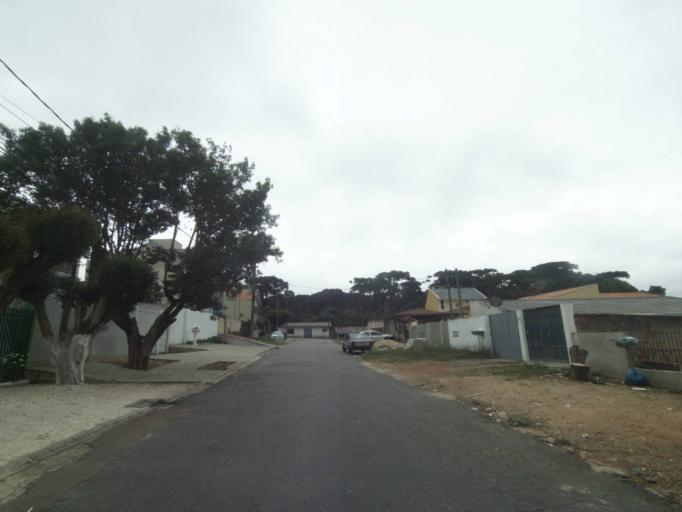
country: BR
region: Parana
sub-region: Sao Jose Dos Pinhais
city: Sao Jose dos Pinhais
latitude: -25.5393
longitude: -49.2877
